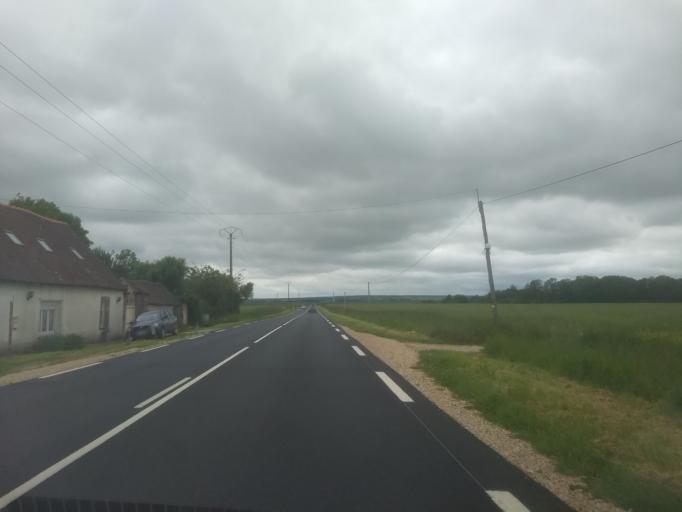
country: FR
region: Centre
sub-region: Departement d'Eure-et-Loir
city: Chateauneuf-en-Thymerais
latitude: 48.5569
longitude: 1.1984
